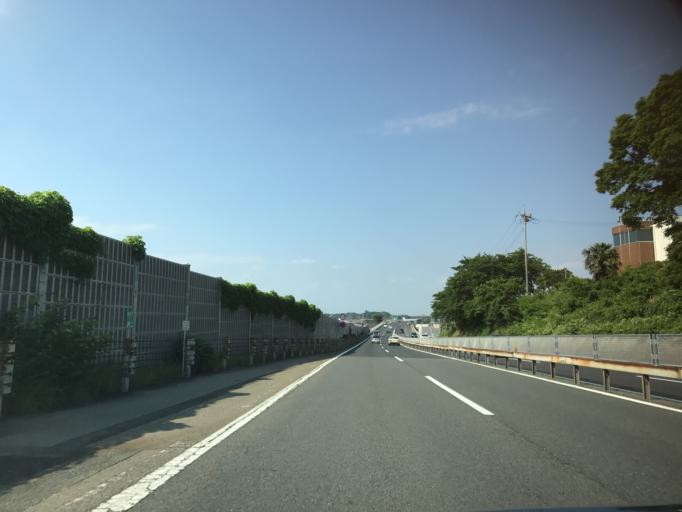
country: JP
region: Kanagawa
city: Isehara
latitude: 35.3546
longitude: 139.3000
